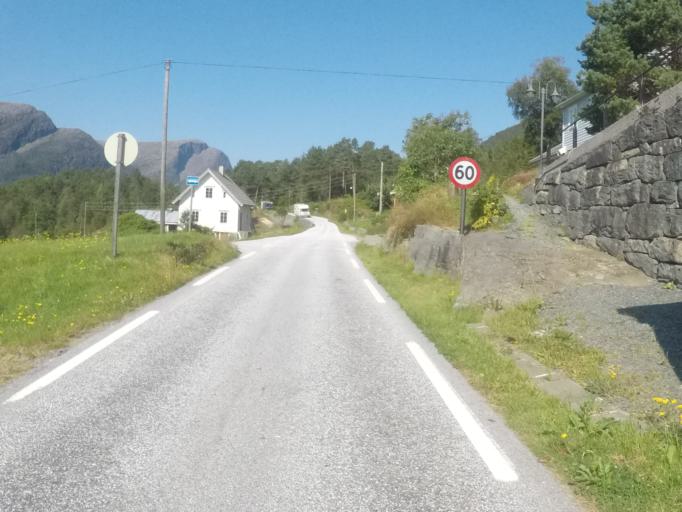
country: NO
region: Sogn og Fjordane
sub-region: Bremanger
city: Svelgen
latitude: 61.7389
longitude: 5.1760
